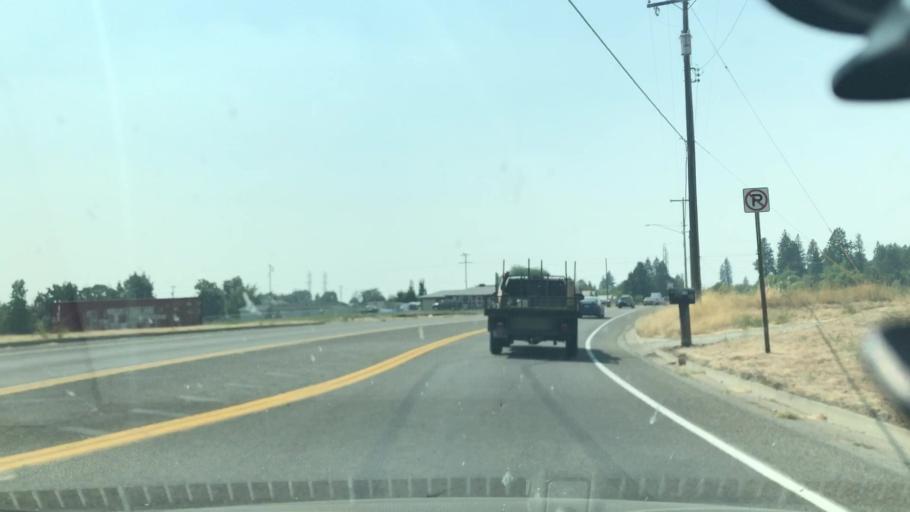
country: US
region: Washington
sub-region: Spokane County
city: Millwood
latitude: 47.6856
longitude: -117.3328
